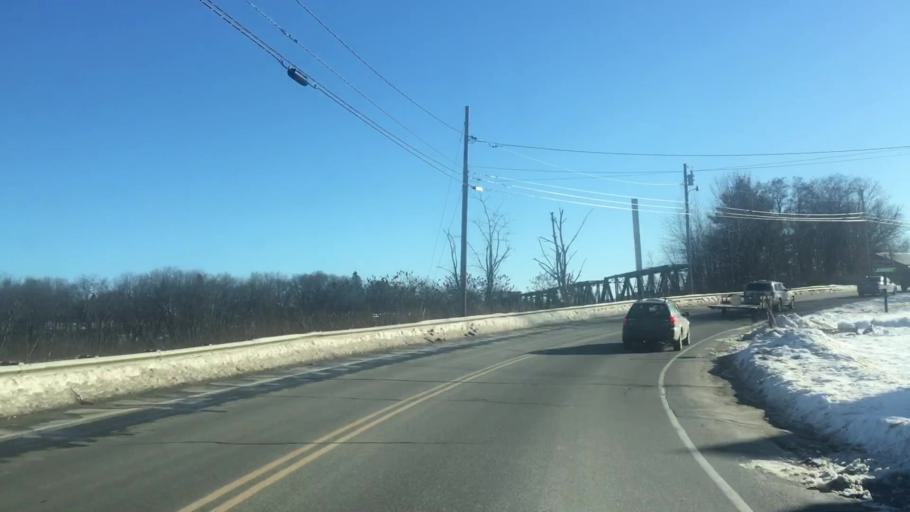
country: US
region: Maine
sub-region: Somerset County
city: Madison
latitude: 44.8026
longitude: -69.8876
